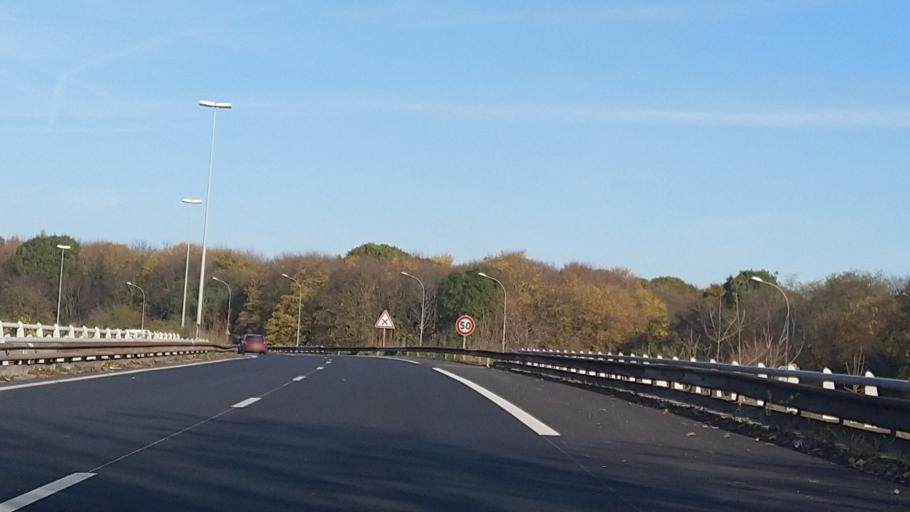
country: FR
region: Ile-de-France
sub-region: Departement de Seine-Saint-Denis
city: La Courneuve
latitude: 48.9350
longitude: 2.3875
